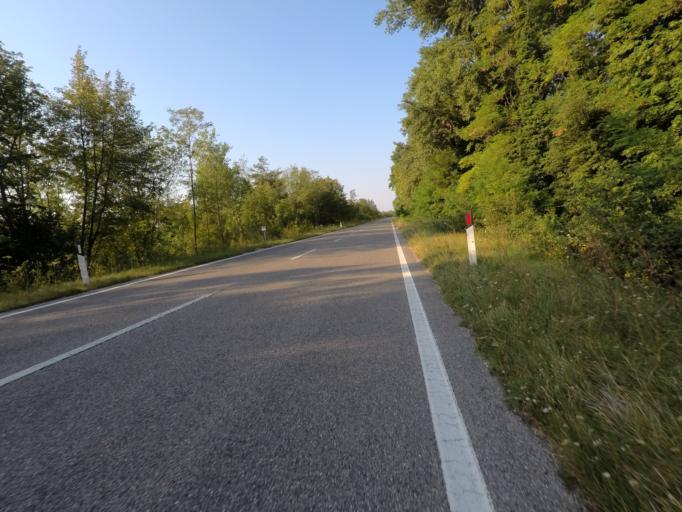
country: IT
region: Friuli Venezia Giulia
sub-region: Provincia di Udine
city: Trasaghis
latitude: 46.2734
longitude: 13.0576
